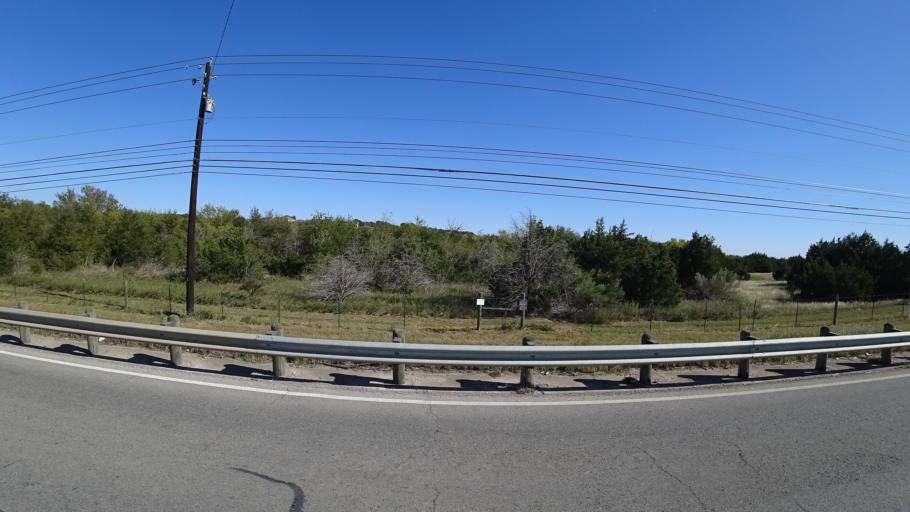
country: US
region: Texas
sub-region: Travis County
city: Hornsby Bend
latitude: 30.2837
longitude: -97.6328
